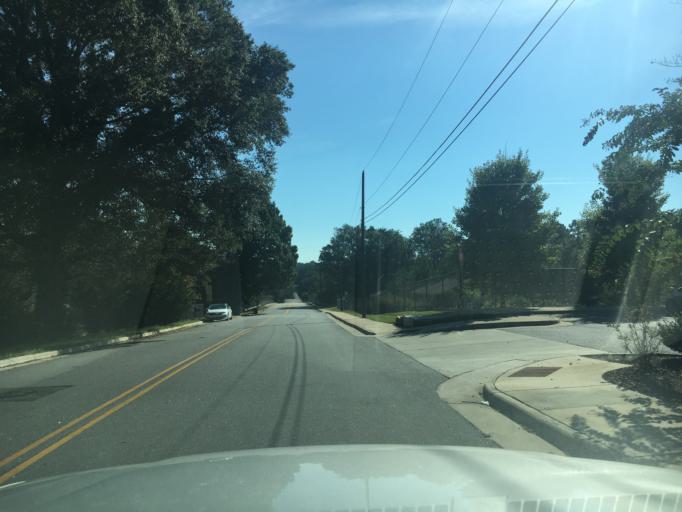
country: US
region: North Carolina
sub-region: Catawba County
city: Hickory
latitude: 35.7244
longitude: -81.3597
